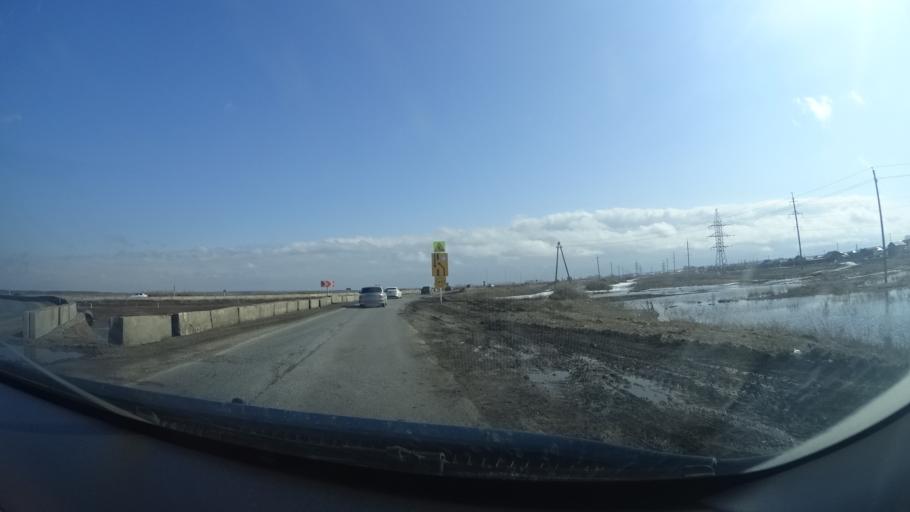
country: RU
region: Bashkortostan
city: Mikhaylovka
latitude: 54.8774
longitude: 55.7155
